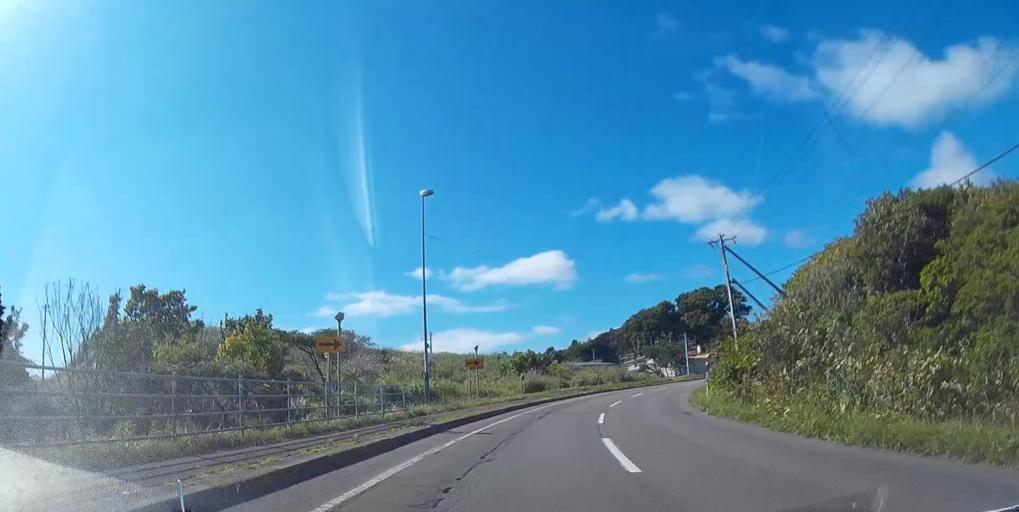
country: JP
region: Hokkaido
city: Kamiiso
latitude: 42.0301
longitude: 140.0967
